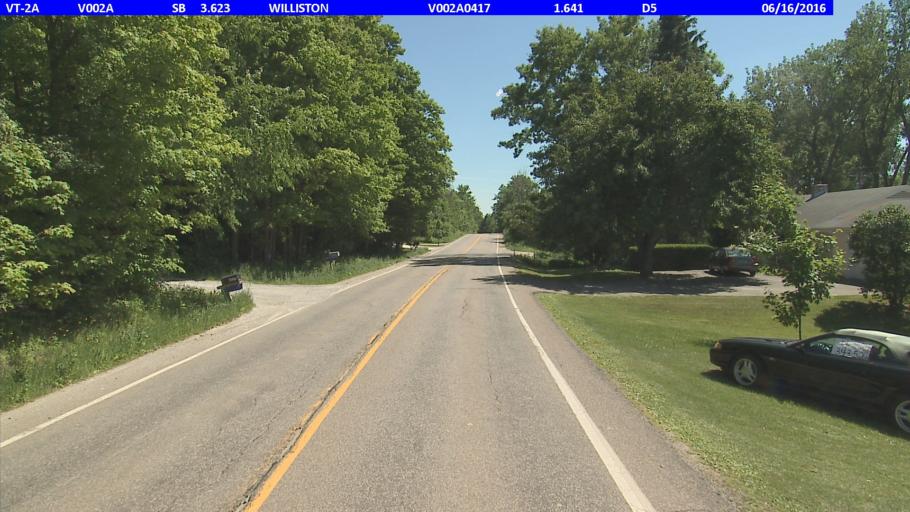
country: US
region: Vermont
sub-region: Chittenden County
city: Williston
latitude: 44.4215
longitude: -73.1240
